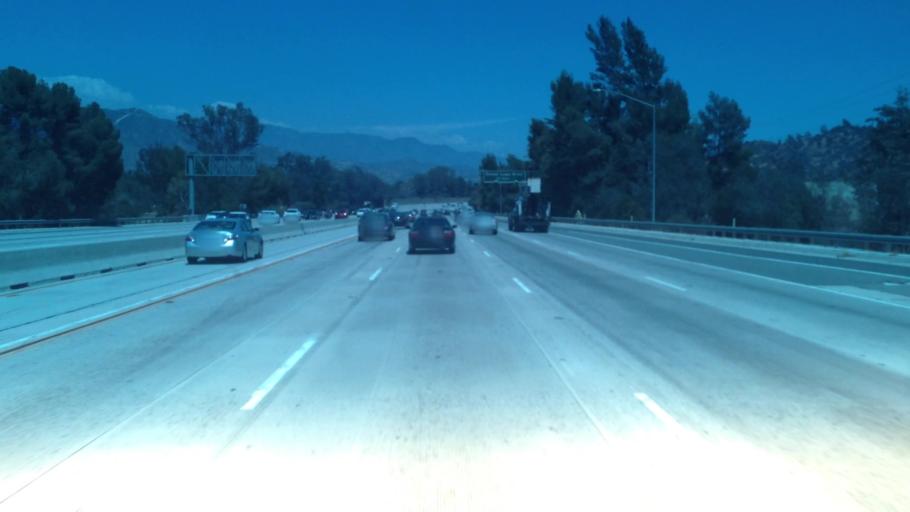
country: US
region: California
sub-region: Los Angeles County
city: Burbank
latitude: 34.1541
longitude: -118.3237
